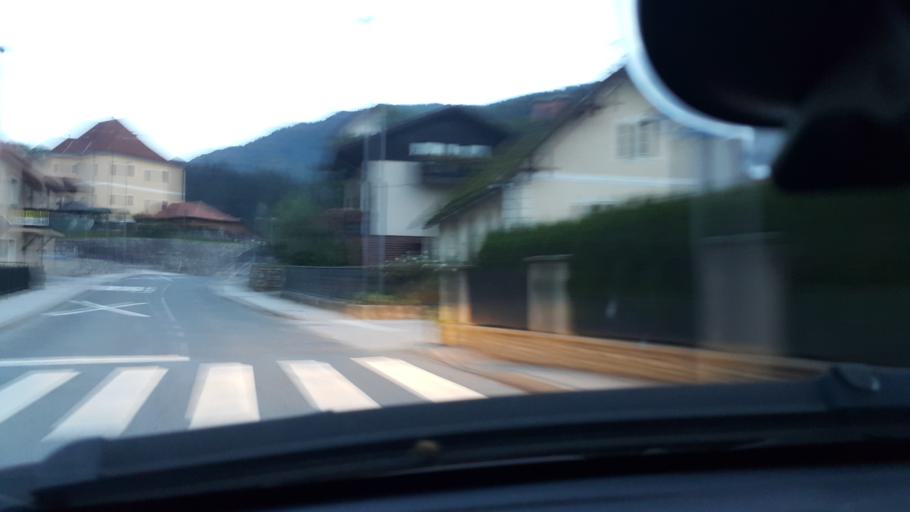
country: SI
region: Vitanje
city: Vitanje
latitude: 46.3832
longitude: 15.2973
